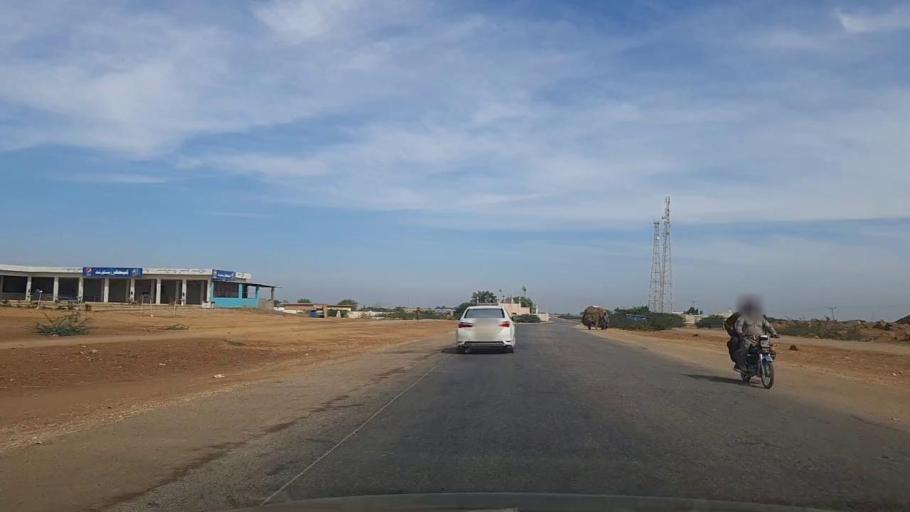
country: PK
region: Sindh
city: Daro Mehar
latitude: 24.8965
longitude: 68.0635
